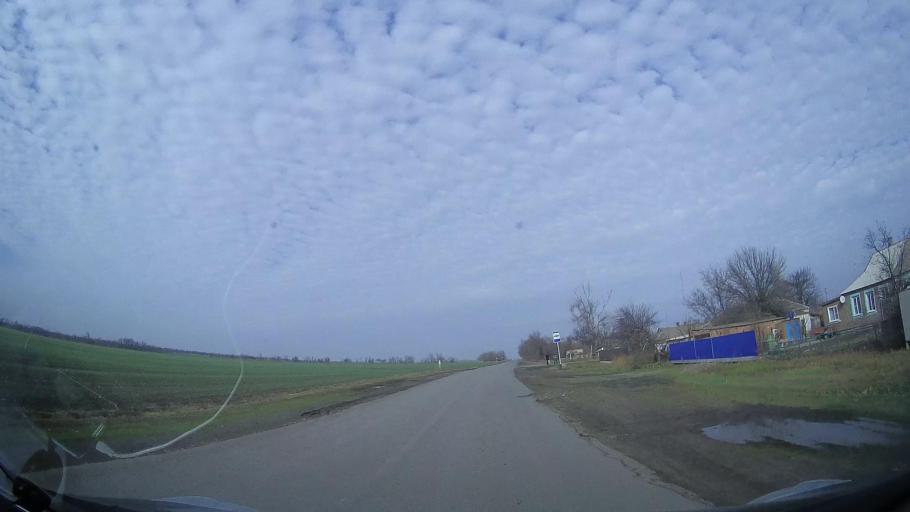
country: RU
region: Rostov
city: Gigant
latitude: 46.9239
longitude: 41.2475
